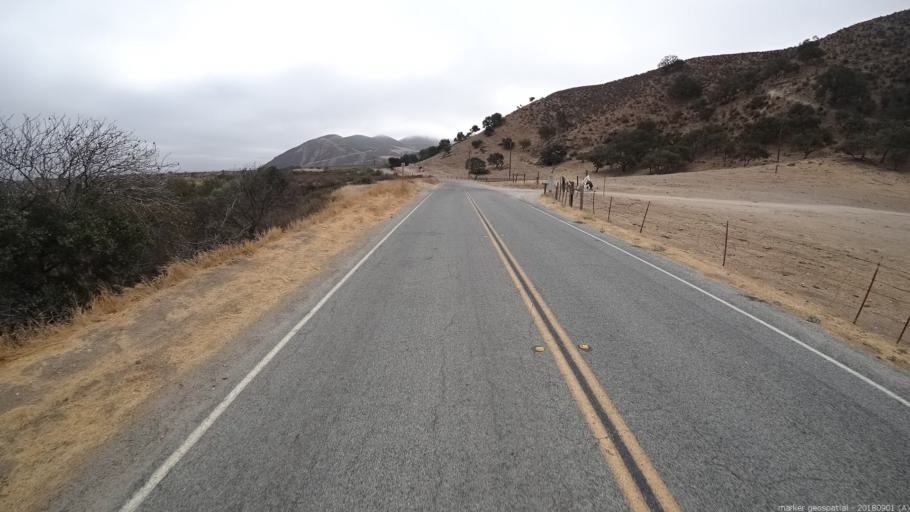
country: US
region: California
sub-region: Monterey County
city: Greenfield
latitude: 36.2794
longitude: -121.3195
